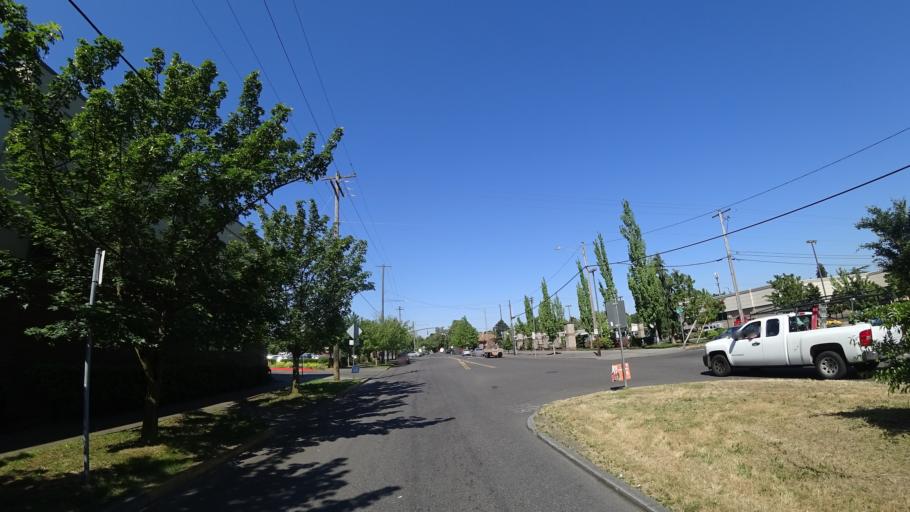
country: US
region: Oregon
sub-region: Multnomah County
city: Portland
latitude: 45.5664
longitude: -122.6602
